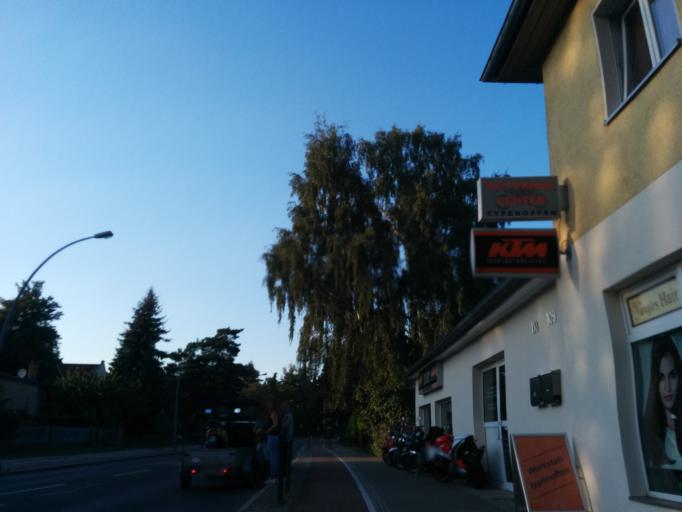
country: DE
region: Berlin
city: Bohnsdorf
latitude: 52.4019
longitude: 13.5739
